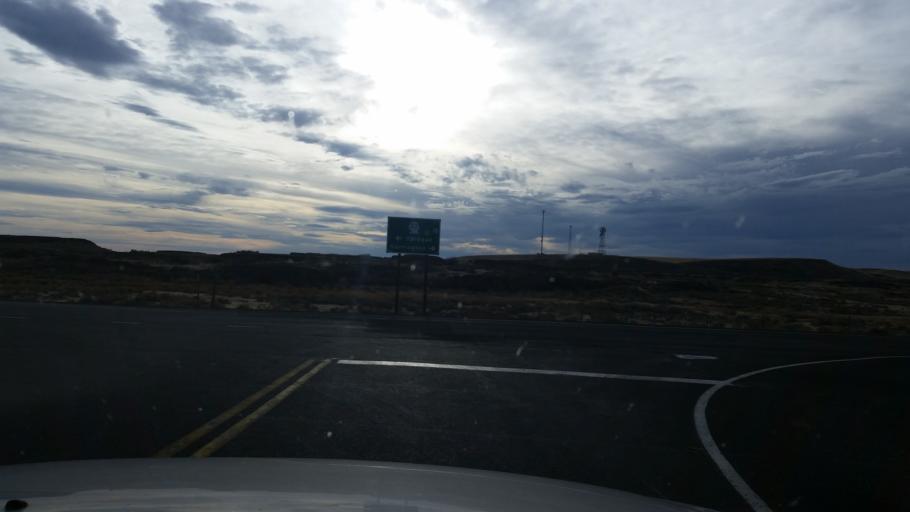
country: US
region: Washington
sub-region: Lincoln County
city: Davenport
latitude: 47.3162
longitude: -117.9741
